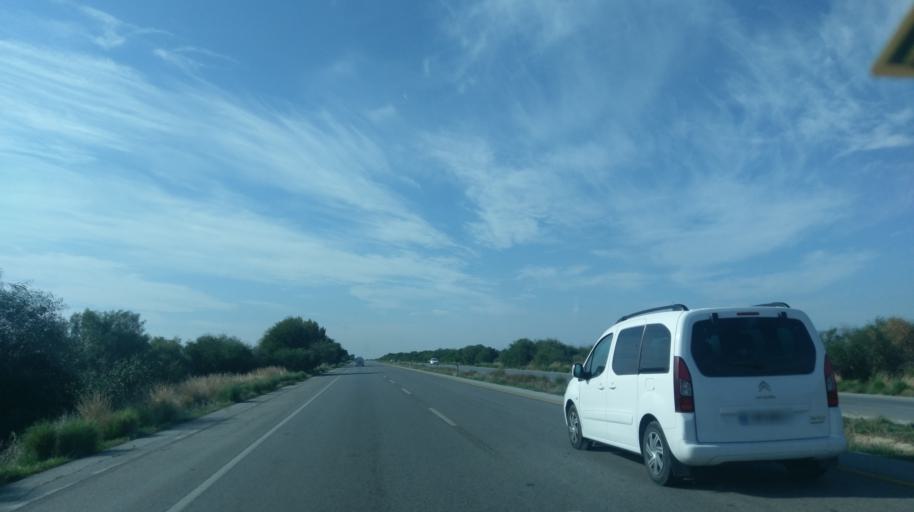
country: CY
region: Ammochostos
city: Lefkonoiko
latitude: 35.1808
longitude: 33.7185
